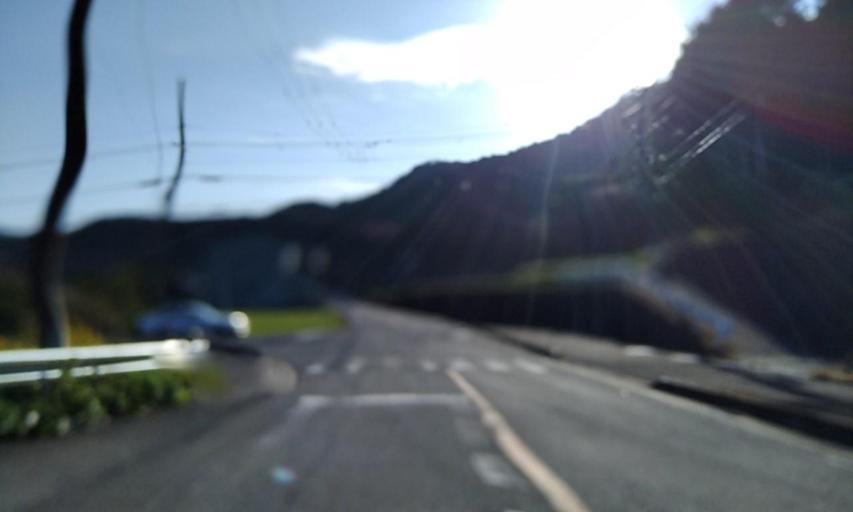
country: JP
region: Wakayama
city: Iwade
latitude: 34.1523
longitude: 135.3116
